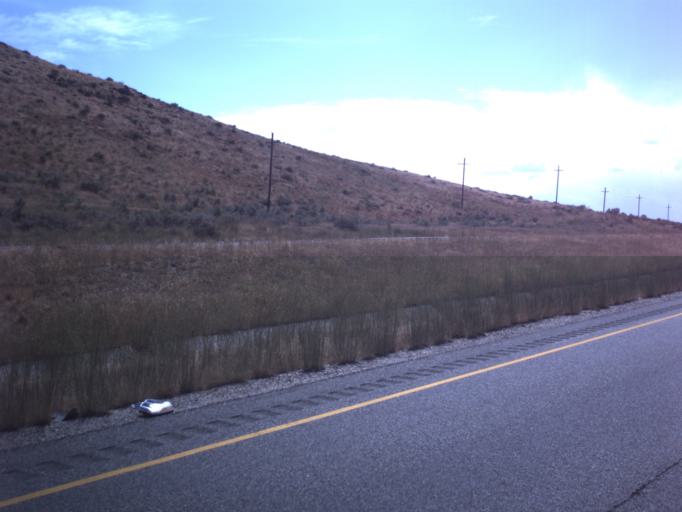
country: US
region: Utah
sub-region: Box Elder County
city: Garland
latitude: 41.8969
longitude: -112.5339
